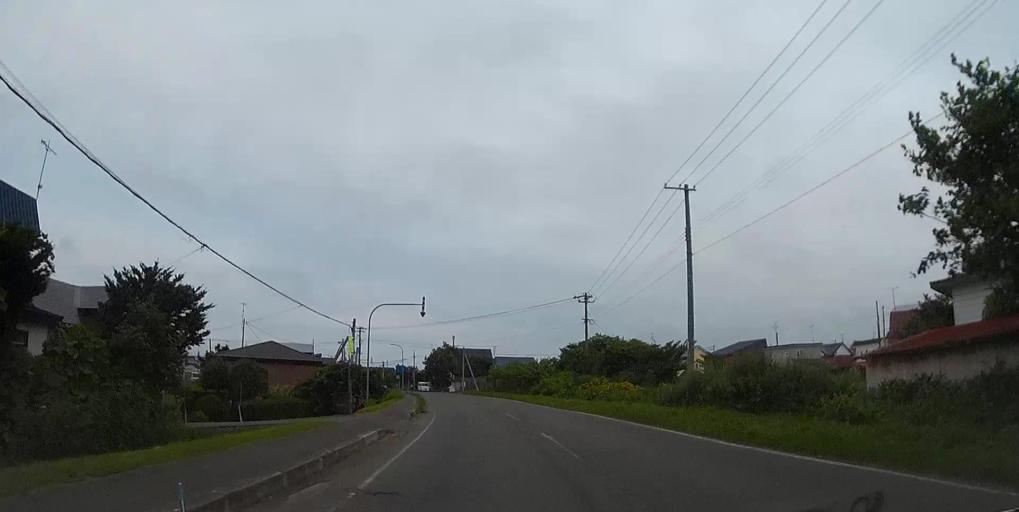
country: JP
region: Hokkaido
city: Nanae
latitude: 42.2542
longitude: 140.2554
